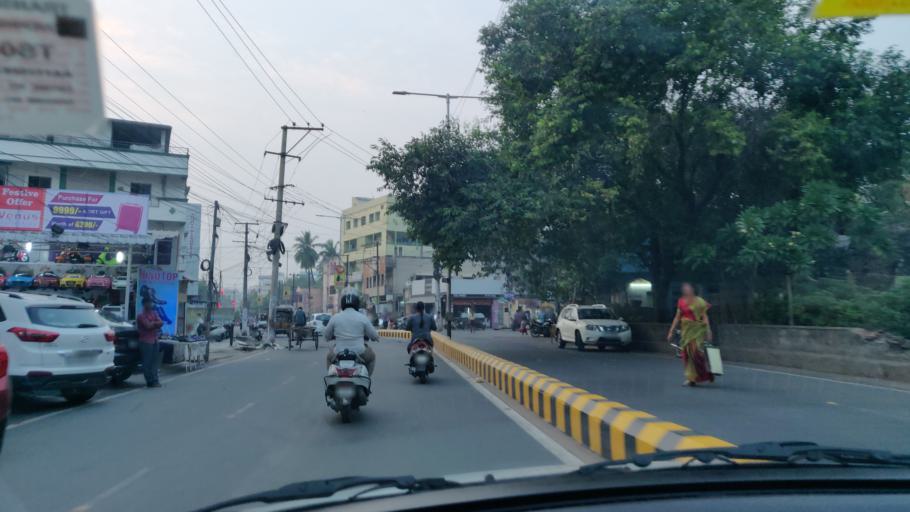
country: IN
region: Andhra Pradesh
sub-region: Krishna
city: Vijayawada
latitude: 16.5065
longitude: 80.6462
